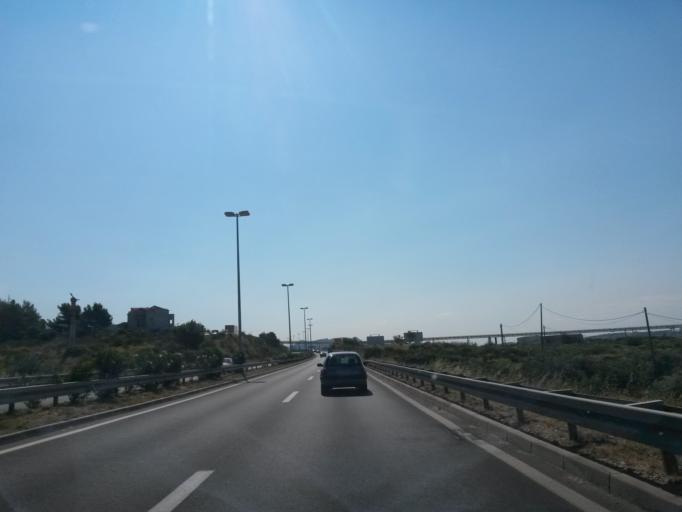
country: HR
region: Splitsko-Dalmatinska
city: Vranjic
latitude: 43.5476
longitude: 16.4436
